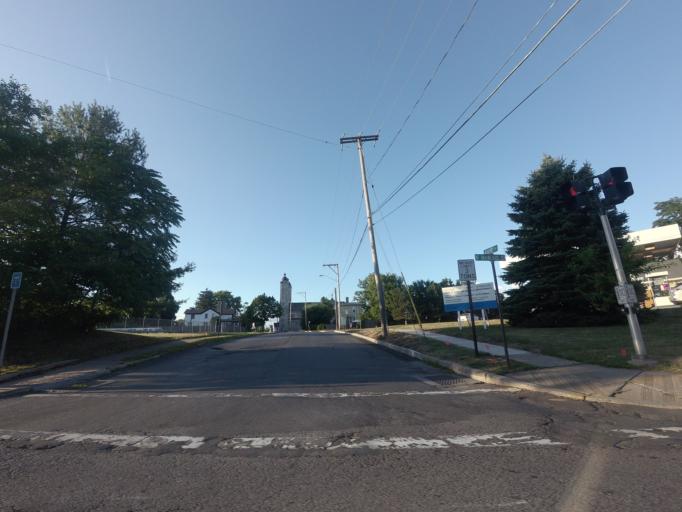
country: US
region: New York
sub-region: Onondaga County
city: East Syracuse
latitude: 43.0647
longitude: -76.0767
